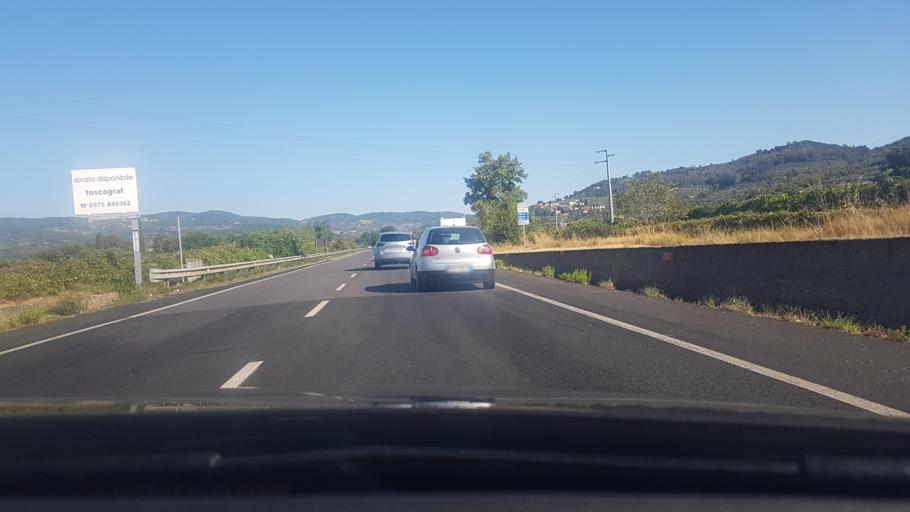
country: IT
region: Tuscany
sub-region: Province of Arezzo
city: Giovi-Ponte alla Chiassa
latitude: 43.5412
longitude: 11.8633
